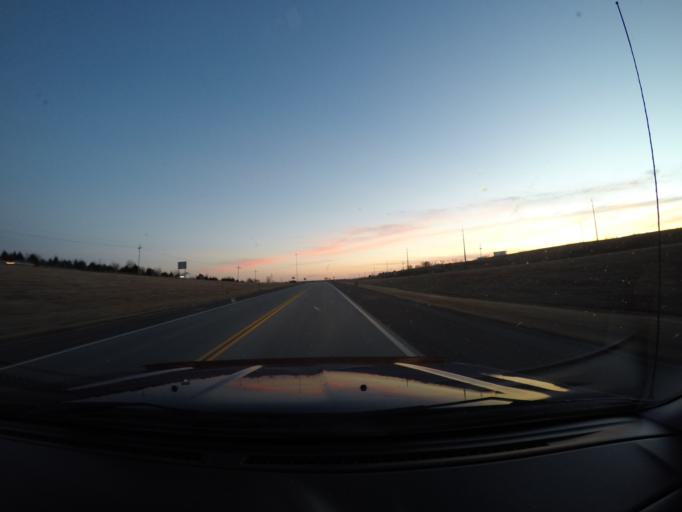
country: US
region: Kansas
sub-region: Douglas County
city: Lawrence
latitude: 38.9707
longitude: -95.3343
